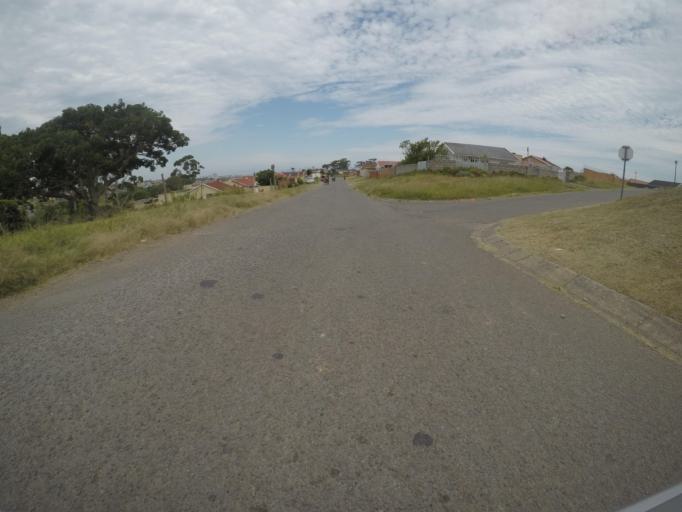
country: ZA
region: Eastern Cape
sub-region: Buffalo City Metropolitan Municipality
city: East London
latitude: -33.0011
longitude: 27.8742
